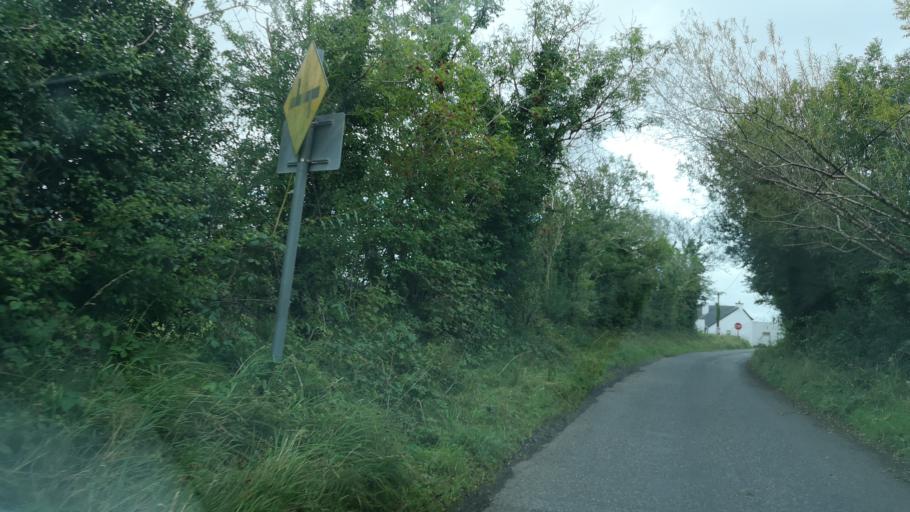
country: IE
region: Connaught
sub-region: County Galway
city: Loughrea
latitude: 53.2965
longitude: -8.5906
